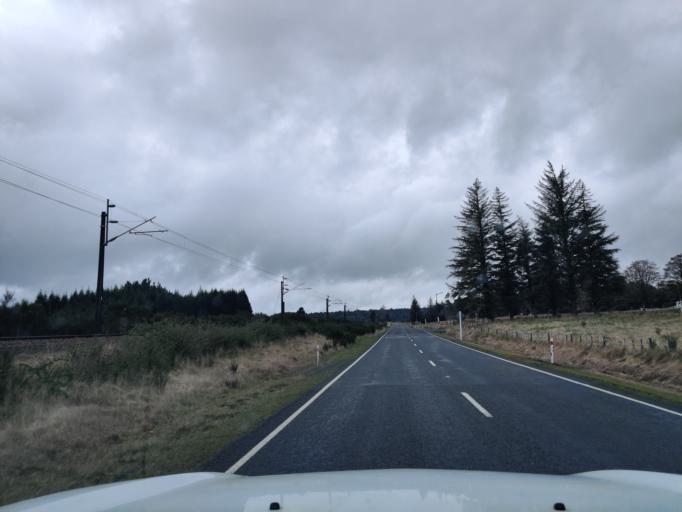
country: NZ
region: Manawatu-Wanganui
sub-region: Ruapehu District
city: Waiouru
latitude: -39.2143
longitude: 175.4006
